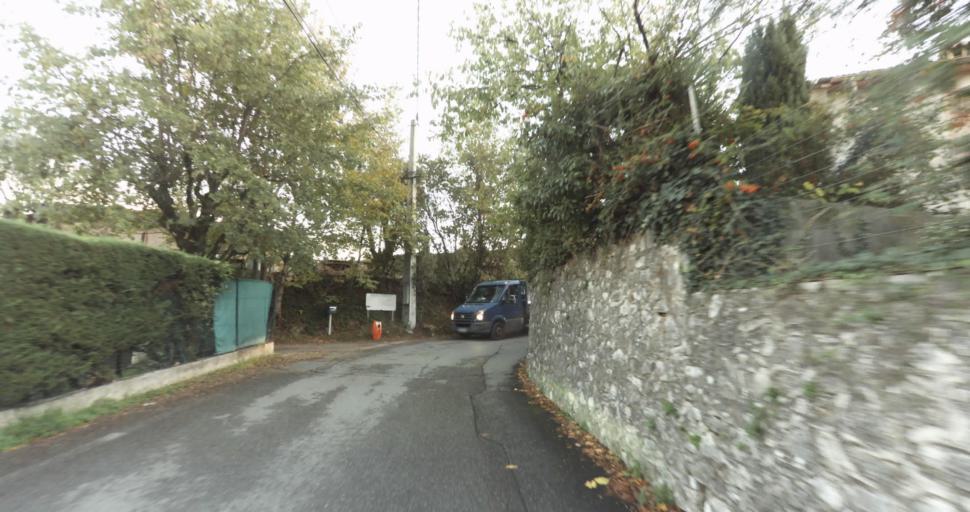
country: FR
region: Provence-Alpes-Cote d'Azur
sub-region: Departement des Alpes-Maritimes
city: Vence
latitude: 43.7323
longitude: 7.1281
